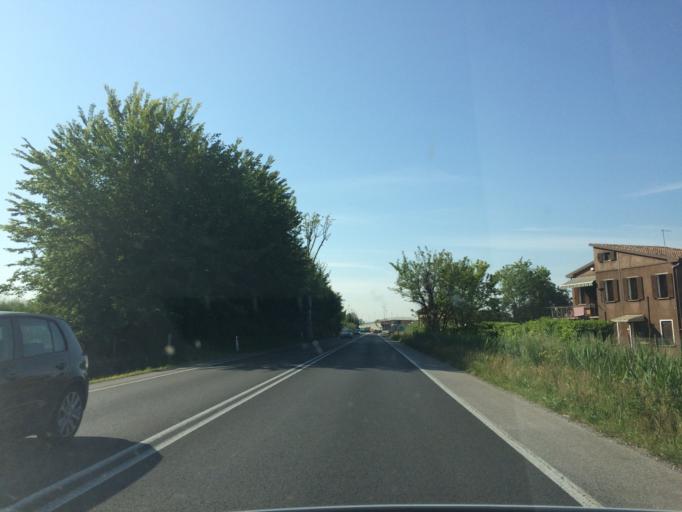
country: IT
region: Veneto
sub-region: Provincia di Padova
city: Santa Maria di Non
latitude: 45.4948
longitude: 11.8311
